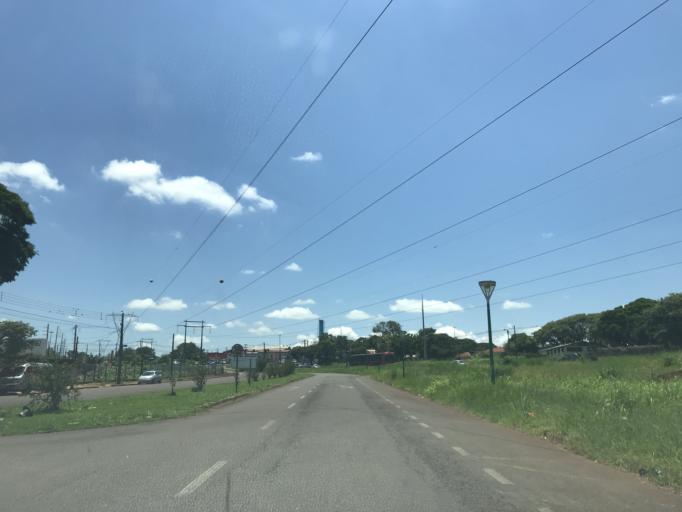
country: BR
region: Parana
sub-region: Maringa
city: Maringa
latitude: -23.4598
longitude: -51.9207
